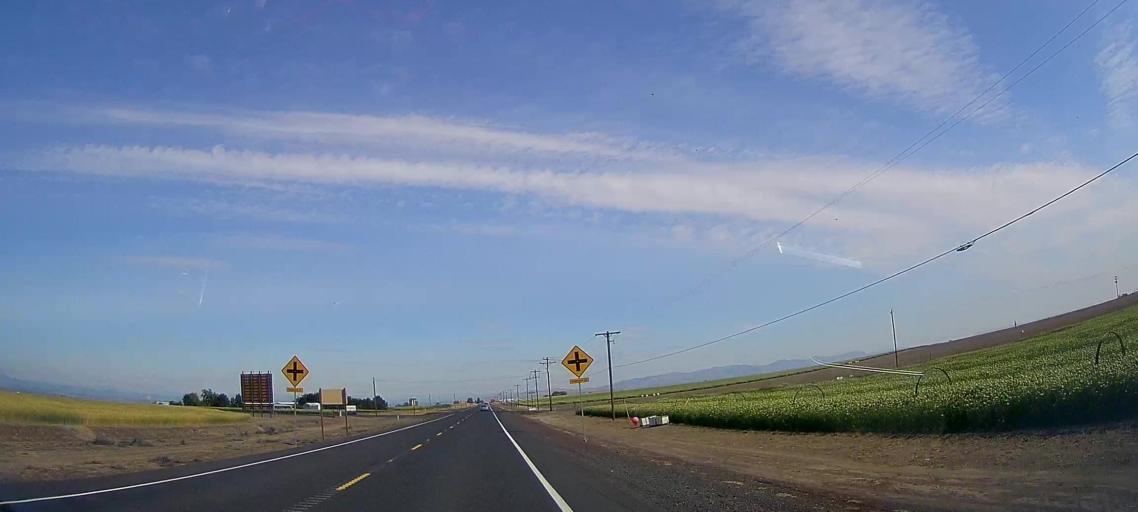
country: US
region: Oregon
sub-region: Jefferson County
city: Madras
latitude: 44.6781
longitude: -121.1457
